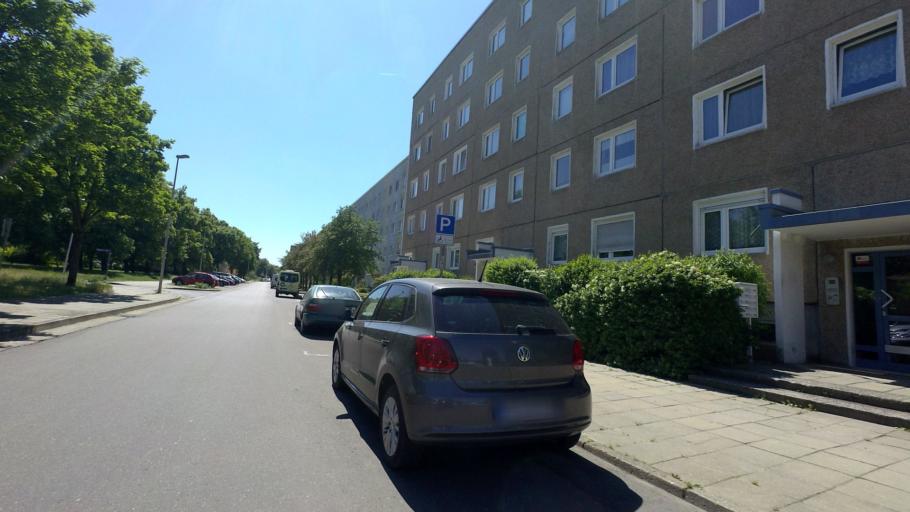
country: DE
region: Brandenburg
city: Cottbus
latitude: 51.7648
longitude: 14.3529
